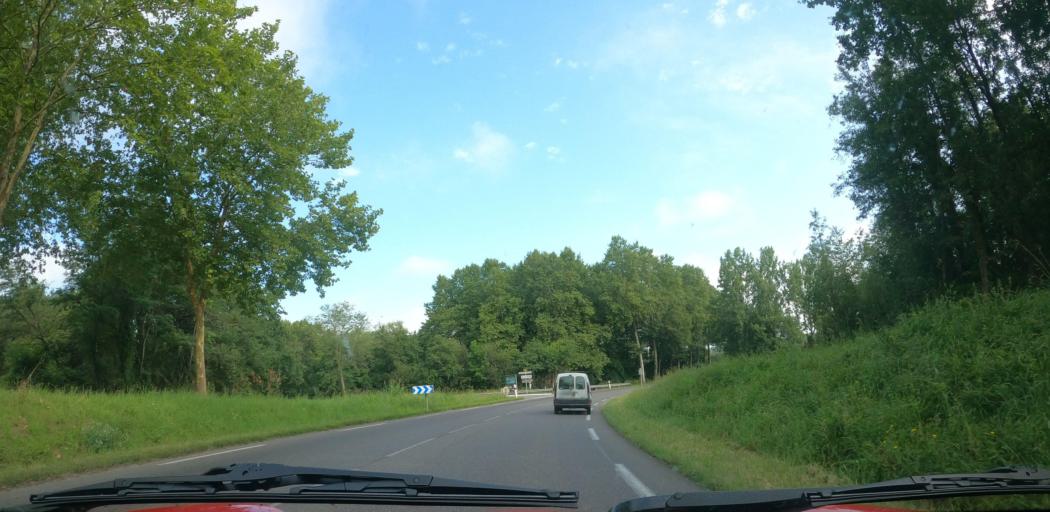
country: FR
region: Aquitaine
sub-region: Departement des Landes
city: Peyrehorade
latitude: 43.5318
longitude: -1.1102
